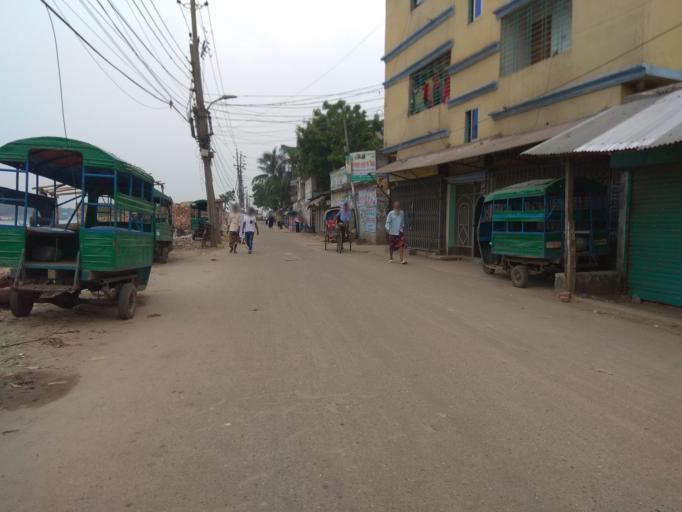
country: BD
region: Dhaka
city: Azimpur
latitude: 23.7128
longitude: 90.3625
